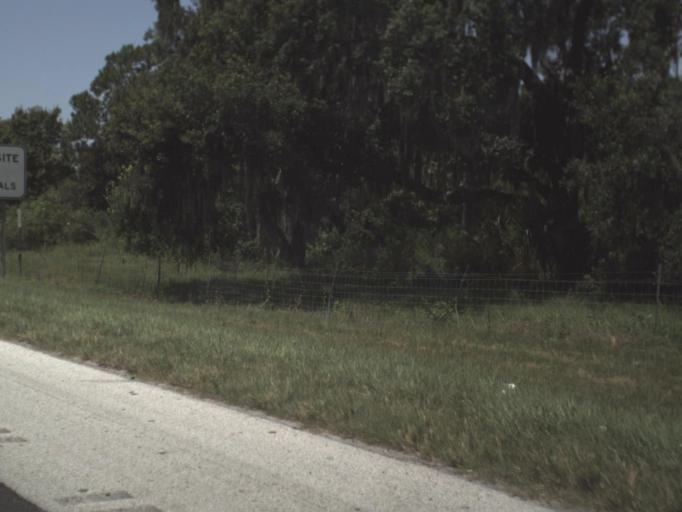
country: US
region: Florida
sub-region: Hillsborough County
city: Dover
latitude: 28.0217
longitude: -82.2524
